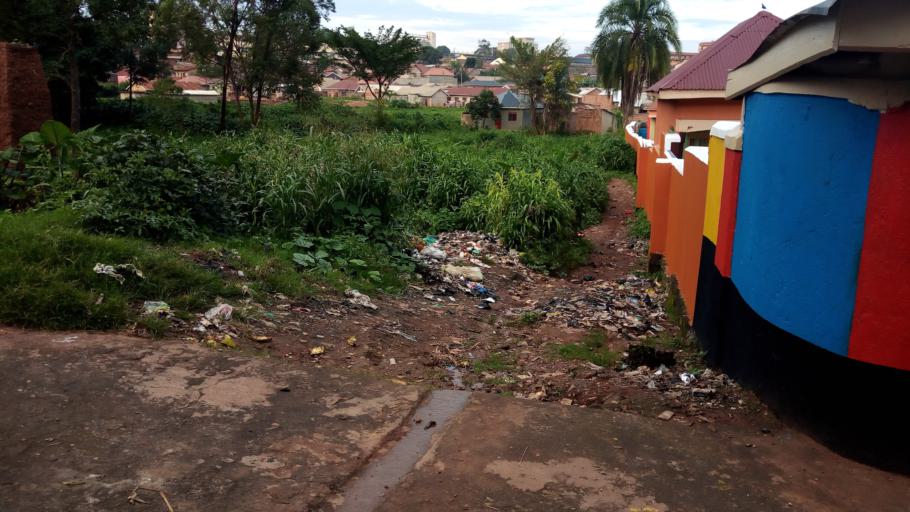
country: UG
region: Central Region
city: Kampala Central Division
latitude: 0.3739
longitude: 32.5534
